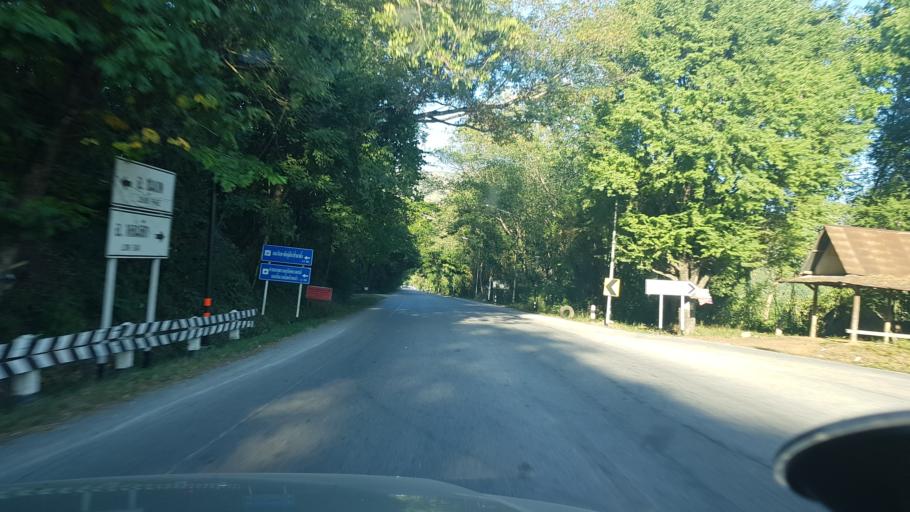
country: TH
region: Khon Kaen
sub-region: Amphoe Phu Pha Man
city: Phu Pha Man
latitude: 16.6495
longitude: 101.8103
